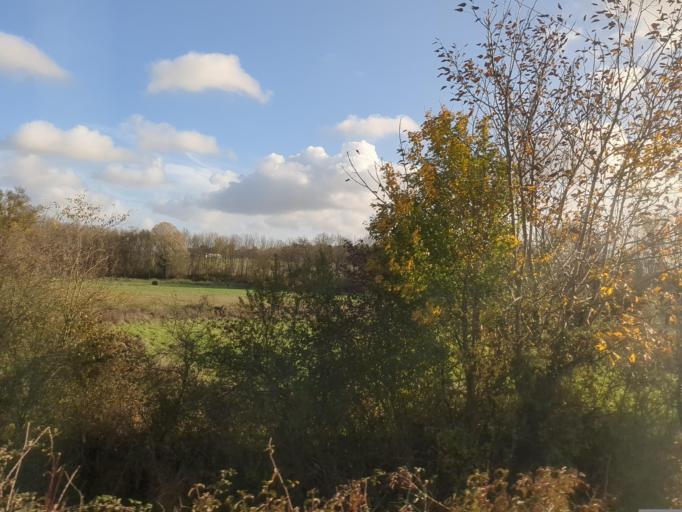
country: FR
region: Centre
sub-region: Departement d'Indre-et-Loire
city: Chanceaux-sur-Choisille
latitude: 47.4531
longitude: 0.6836
